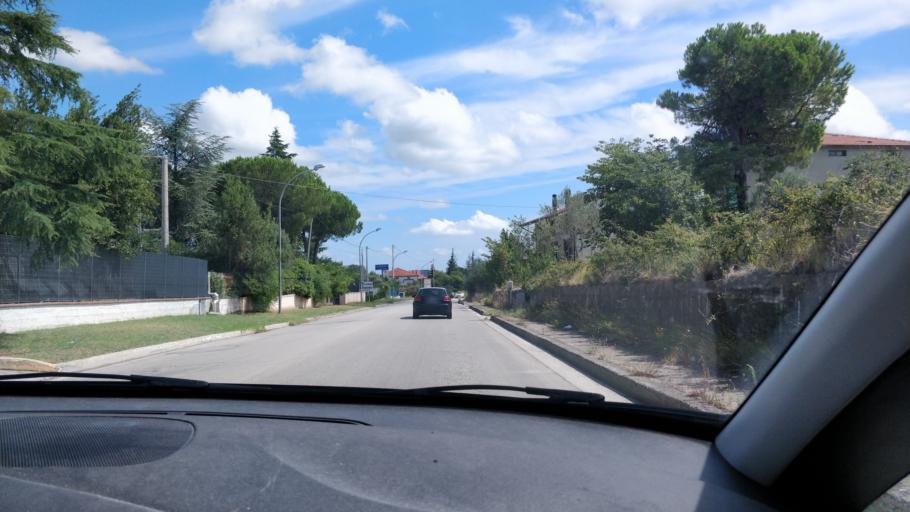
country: IT
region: Abruzzo
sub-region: Provincia di Chieti
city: Treglio
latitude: 42.2448
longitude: 14.4153
